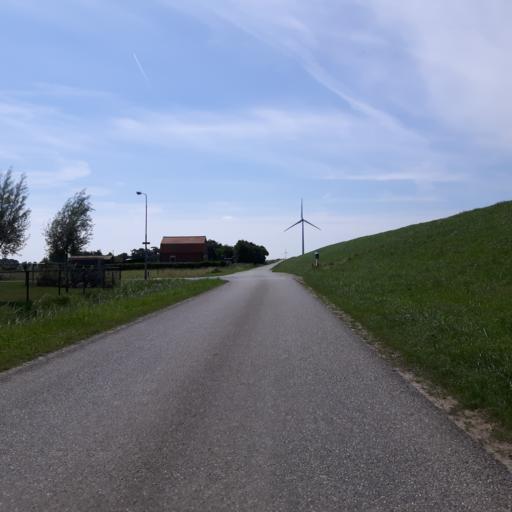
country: NL
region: Zeeland
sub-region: Schouwen-Duiveland
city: Bruinisse
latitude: 51.6459
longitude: 4.1105
